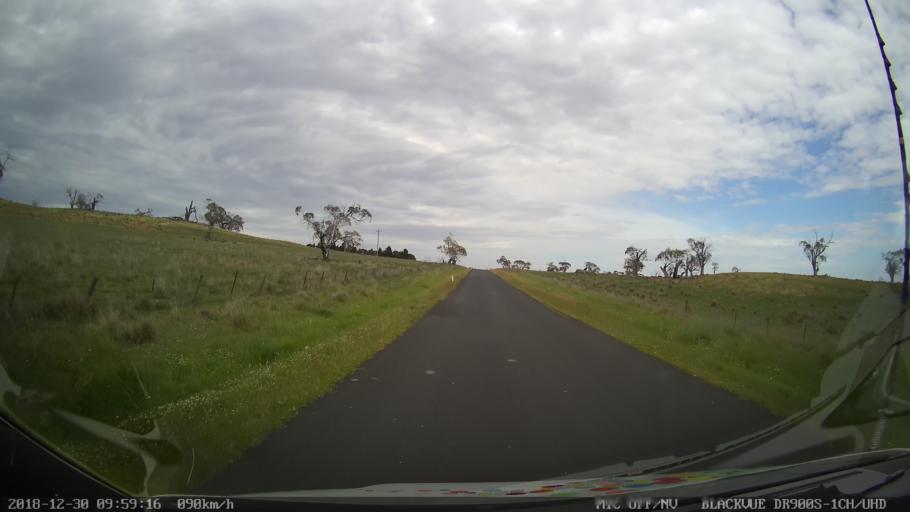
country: AU
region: New South Wales
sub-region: Cooma-Monaro
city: Cooma
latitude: -36.5228
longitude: 149.2128
